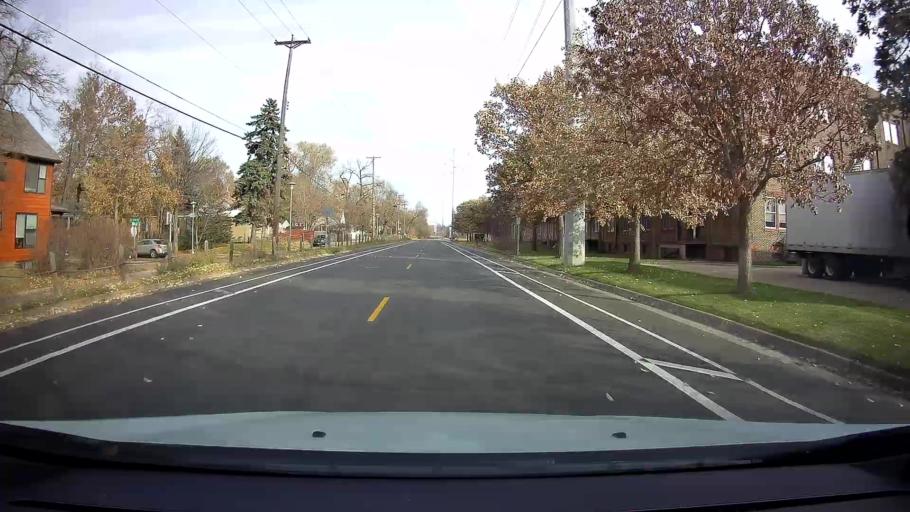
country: US
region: Minnesota
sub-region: Ramsey County
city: Lauderdale
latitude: 44.9843
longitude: -93.2208
